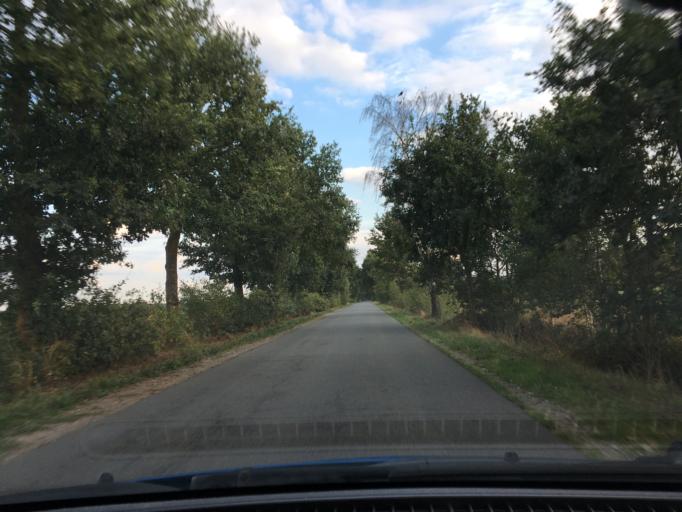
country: DE
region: Lower Saxony
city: Vierhofen
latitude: 53.2779
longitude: 10.1979
